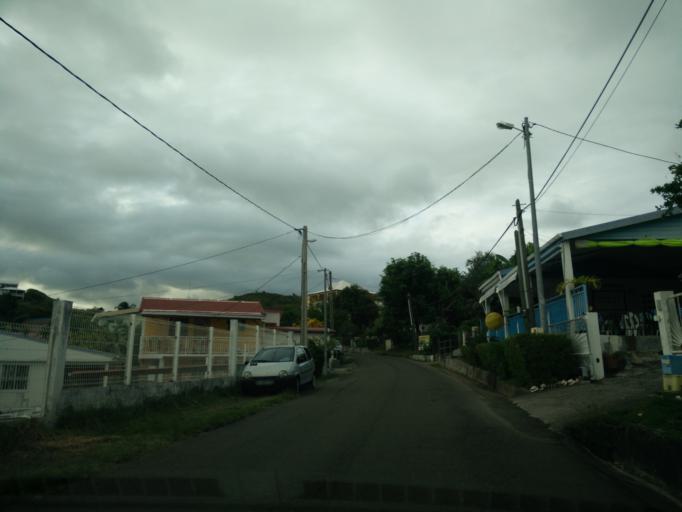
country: MQ
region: Martinique
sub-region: Martinique
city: Le Marin
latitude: 14.4439
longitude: -60.8354
